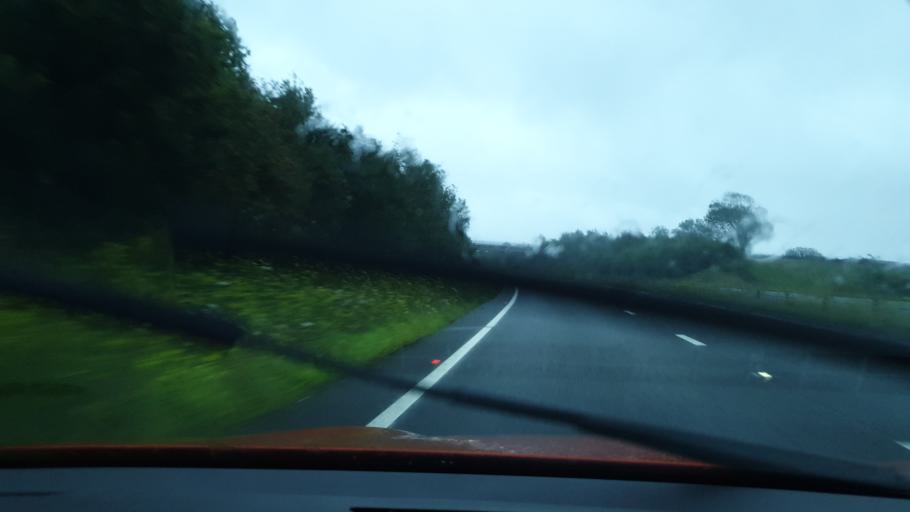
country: GB
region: England
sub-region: Cumbria
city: Grange-over-Sands
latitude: 54.2385
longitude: -2.9253
